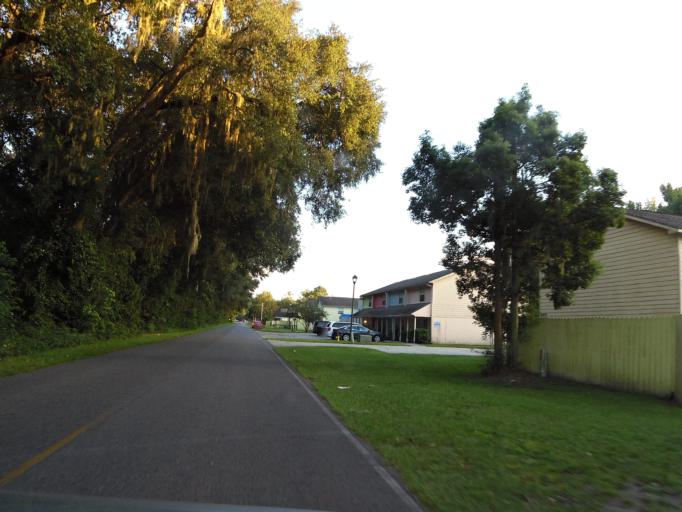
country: US
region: Georgia
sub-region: Camden County
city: Kingsland
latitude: 30.7979
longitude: -81.6913
